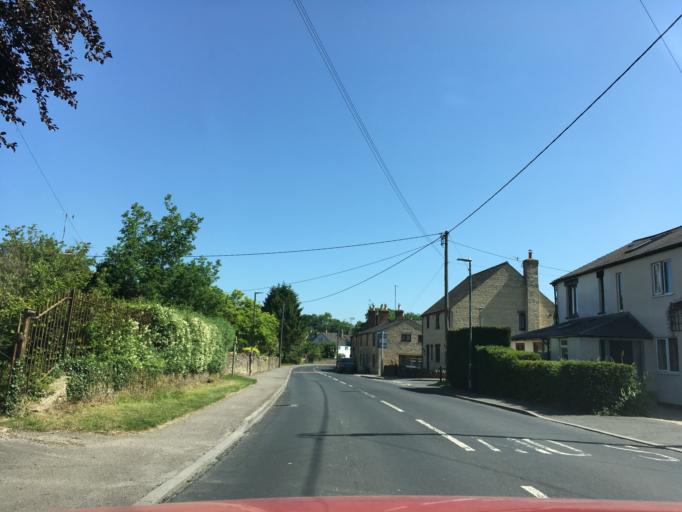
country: GB
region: England
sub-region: Gloucestershire
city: Shipton Village
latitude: 51.8737
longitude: -1.9677
